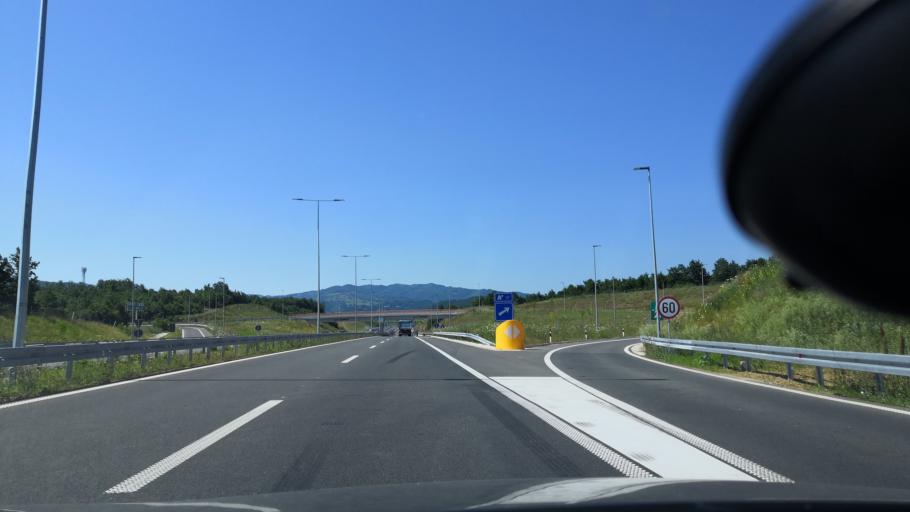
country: RS
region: Central Serbia
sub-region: Pcinjski Okrug
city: Vladicin Han
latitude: 42.7020
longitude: 22.0752
